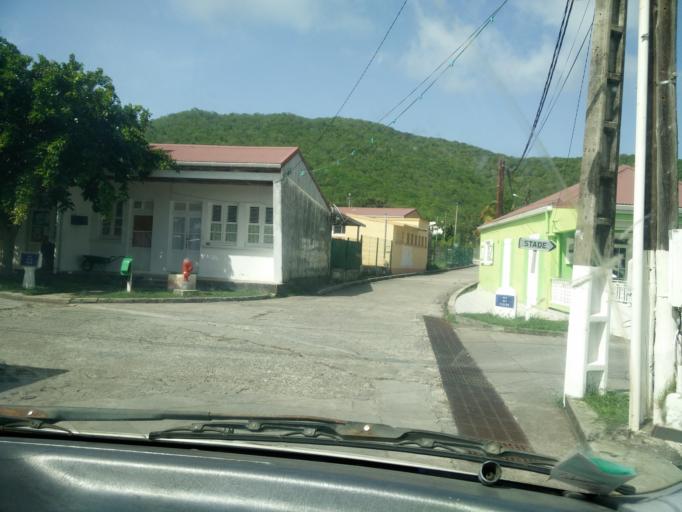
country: GP
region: Guadeloupe
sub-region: Guadeloupe
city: Terre-de-Bas
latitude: 15.8497
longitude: -61.6430
